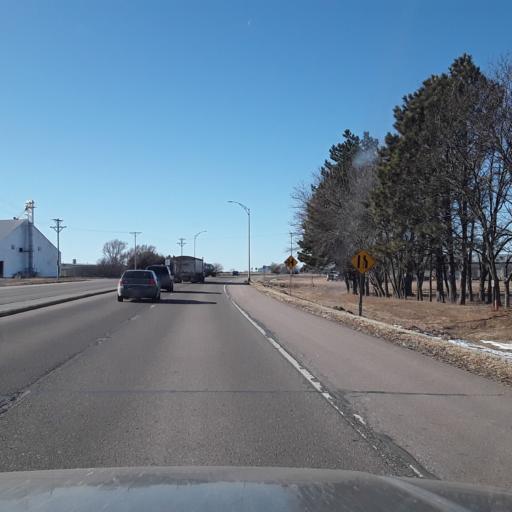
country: US
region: Nebraska
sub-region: Kearney County
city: Minden
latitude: 40.5021
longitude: -98.9591
